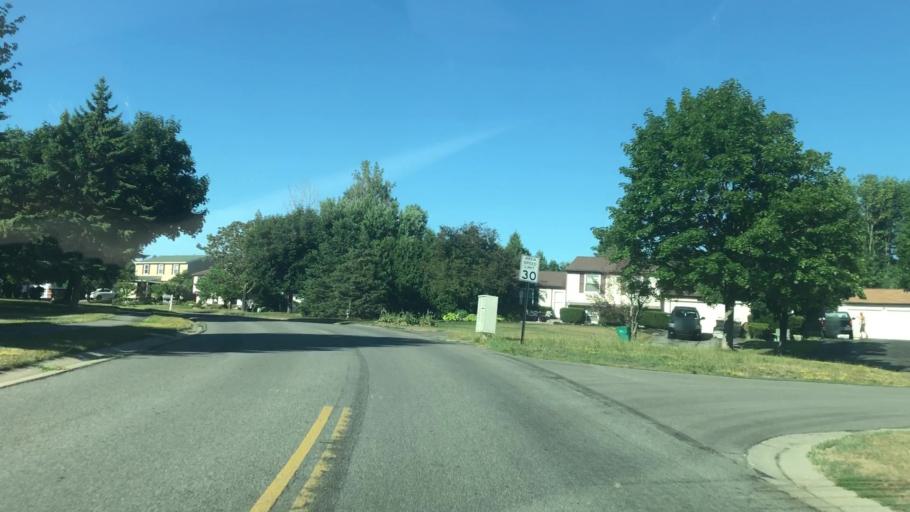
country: US
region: New York
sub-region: Wayne County
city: Macedon
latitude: 43.1241
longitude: -77.2996
